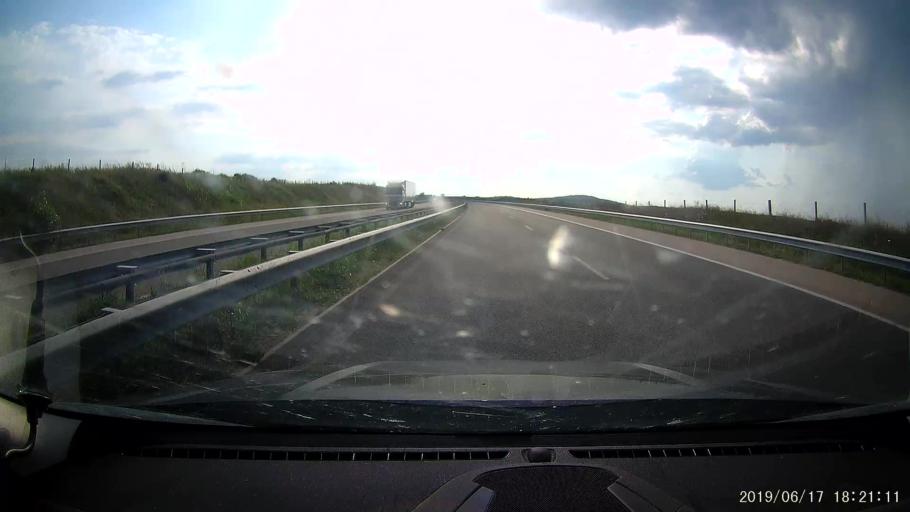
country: BG
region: Khaskovo
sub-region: Obshtina Simeonovgrad
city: Simeonovgrad
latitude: 41.9670
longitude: 25.7910
